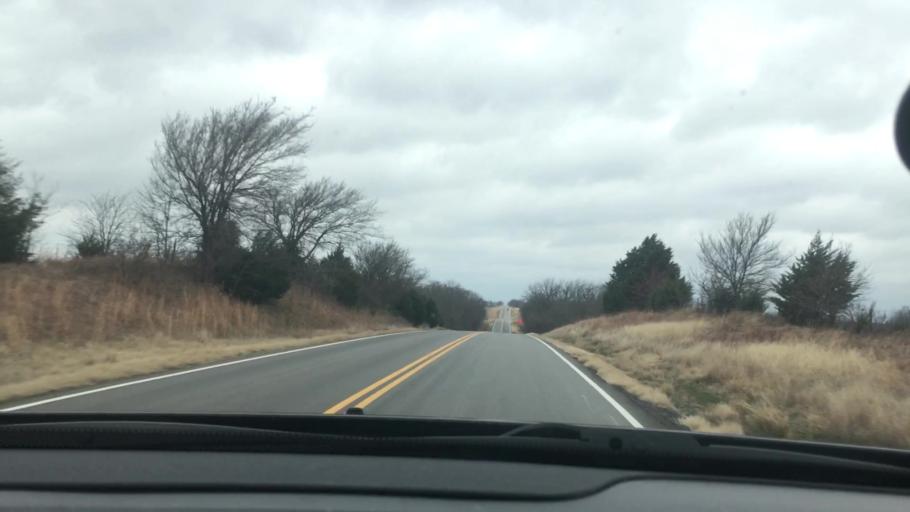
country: US
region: Oklahoma
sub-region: Atoka County
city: Atoka
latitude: 34.3750
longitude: -96.2079
